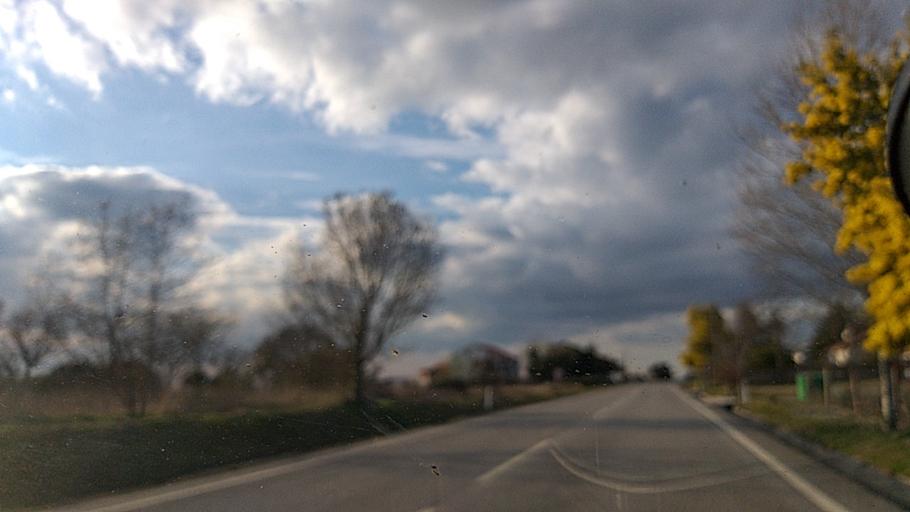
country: ES
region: Castille and Leon
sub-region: Provincia de Salamanca
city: Aldea del Obispo
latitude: 40.7043
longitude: -6.8949
